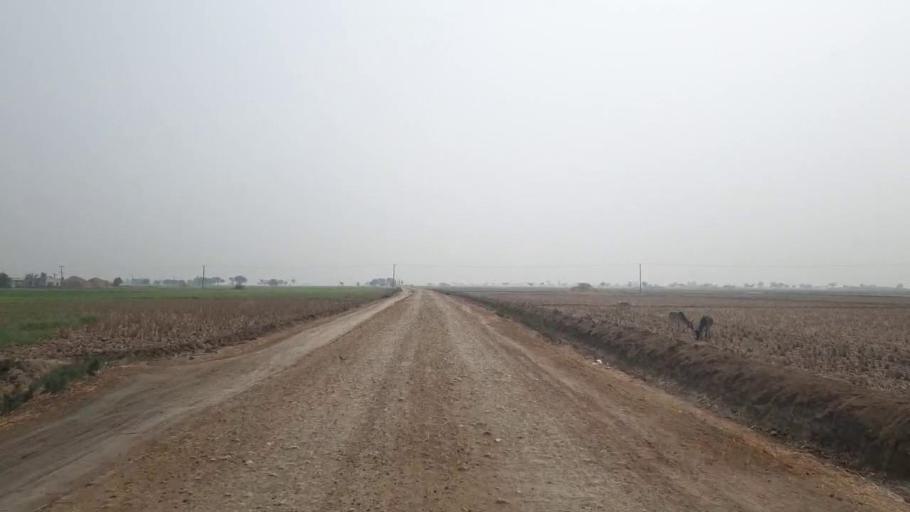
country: PK
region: Sindh
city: Kario
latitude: 24.6485
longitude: 68.5952
